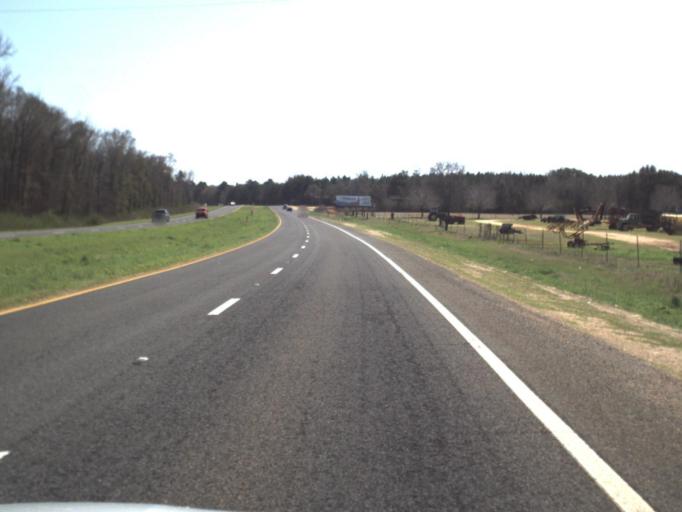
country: US
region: Florida
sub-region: Jackson County
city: Graceville
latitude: 30.9719
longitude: -85.4092
